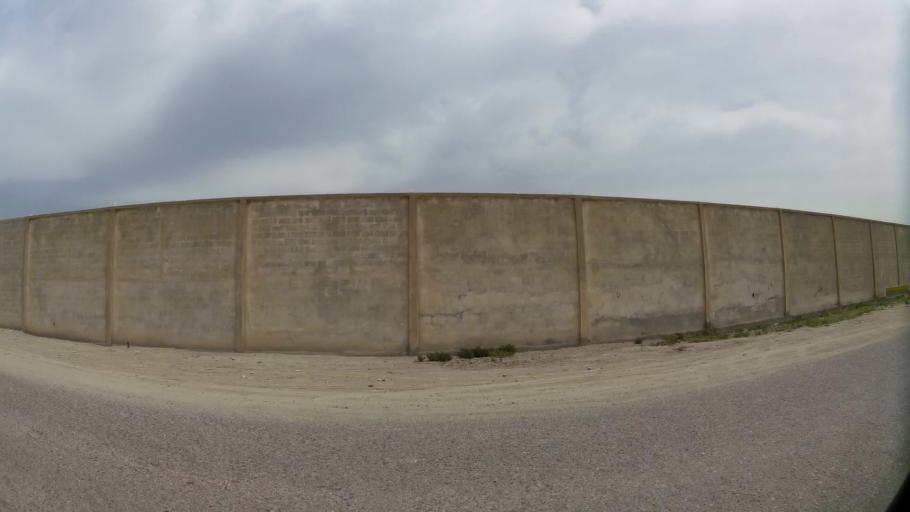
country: QA
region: Baladiyat ar Rayyan
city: Ar Rayyan
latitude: 25.2769
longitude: 51.4605
